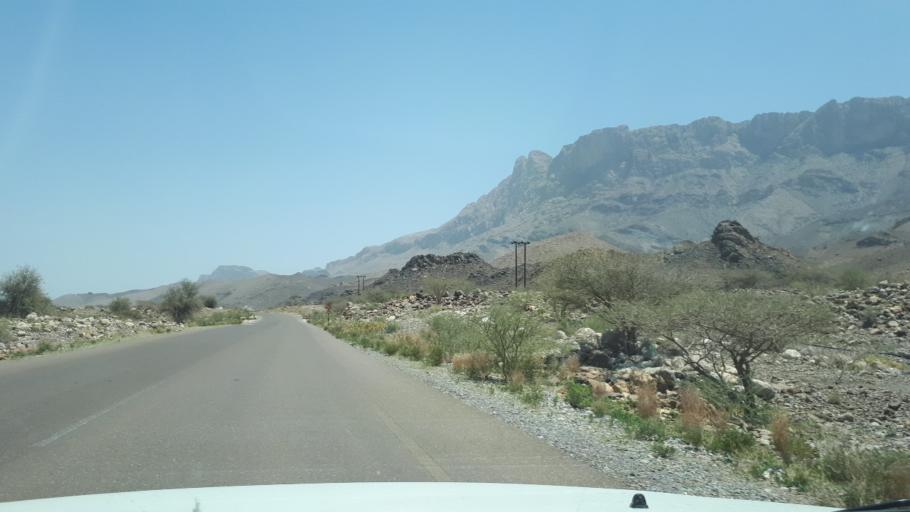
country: OM
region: Muhafazat ad Dakhiliyah
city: Bahla'
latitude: 23.1641
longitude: 57.1623
